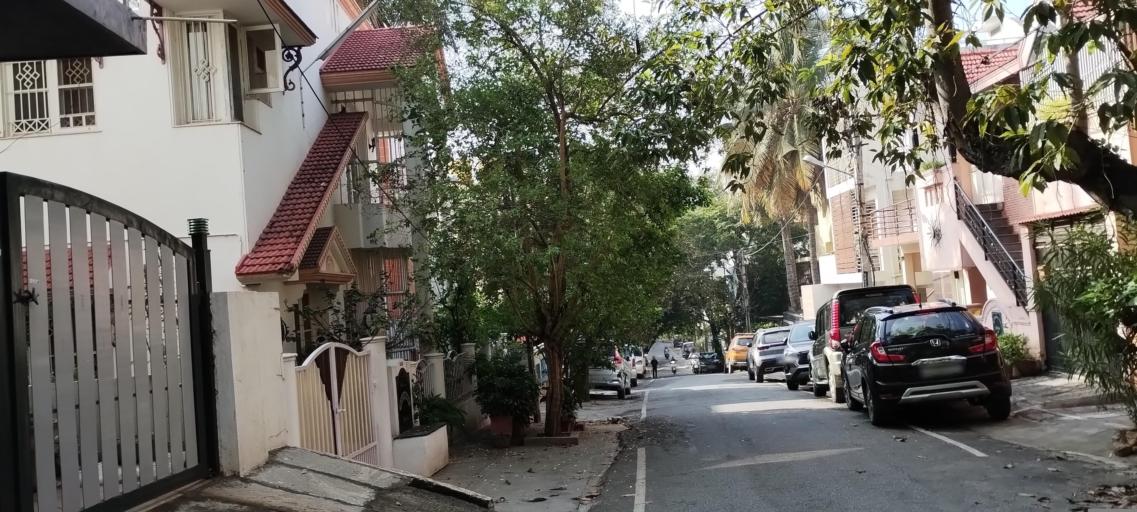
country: IN
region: Karnataka
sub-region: Bangalore Urban
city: Bangalore
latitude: 12.9370
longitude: 77.5459
